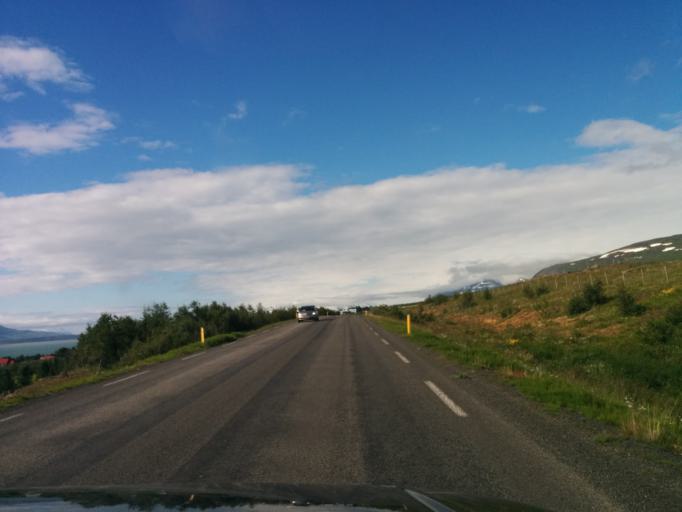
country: IS
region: Northeast
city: Akureyri
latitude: 65.7409
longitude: -18.0741
